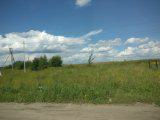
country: RU
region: Moskovskaya
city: Ramenskoye
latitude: 55.5799
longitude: 38.2710
